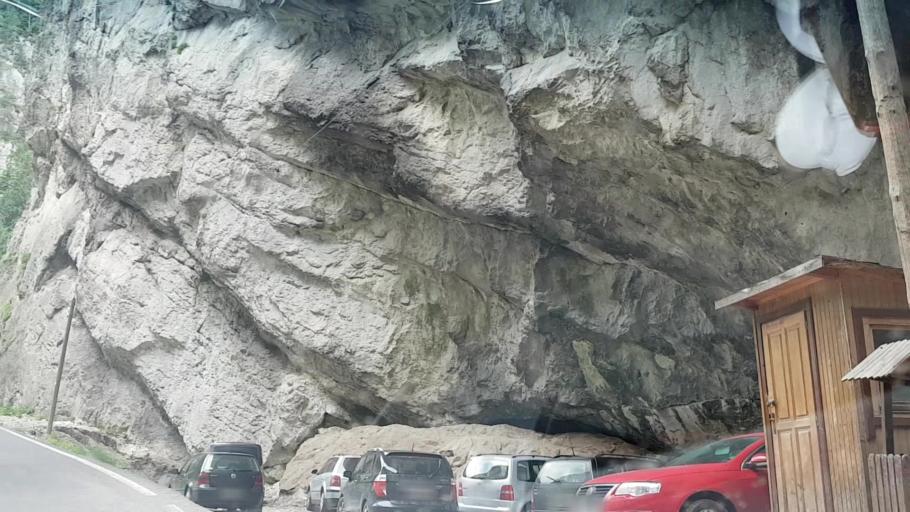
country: RO
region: Neamt
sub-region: Comuna Bicaz Chei
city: Bicaz Chei
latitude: 46.8118
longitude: 25.8270
